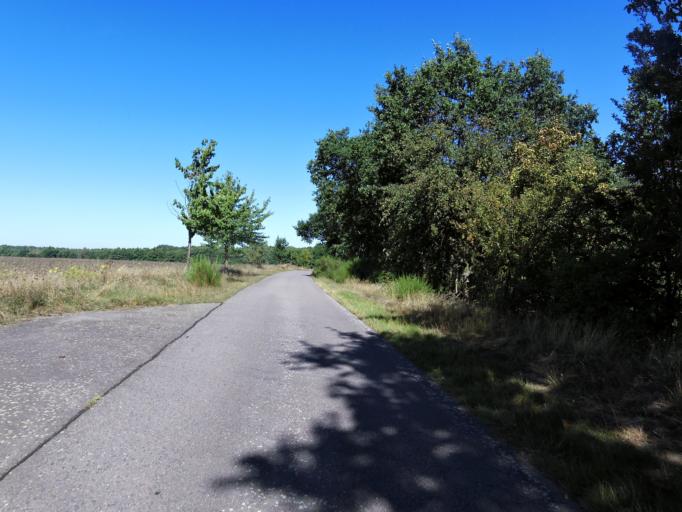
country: DE
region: Saxony-Anhalt
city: Pretzsch
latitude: 51.6712
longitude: 12.8289
